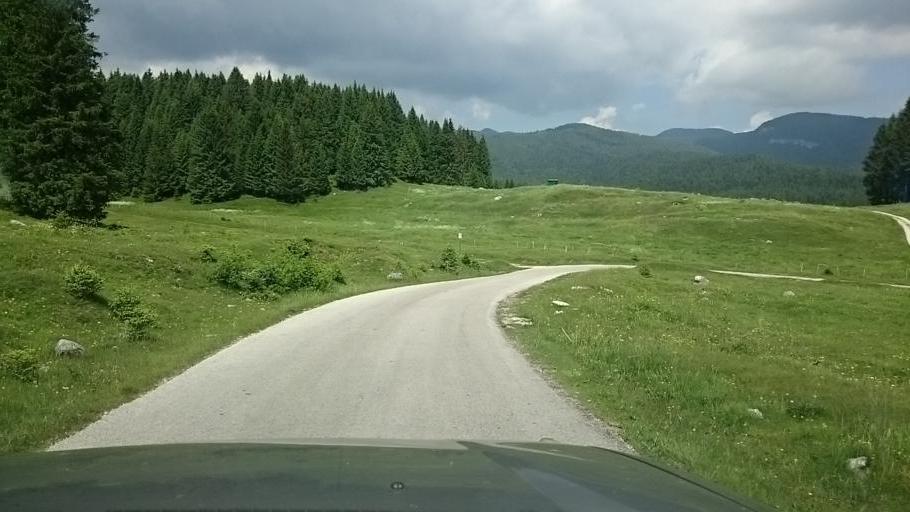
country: IT
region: Trentino-Alto Adige
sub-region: Provincia di Trento
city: Grigno
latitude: 45.9767
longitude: 11.5945
